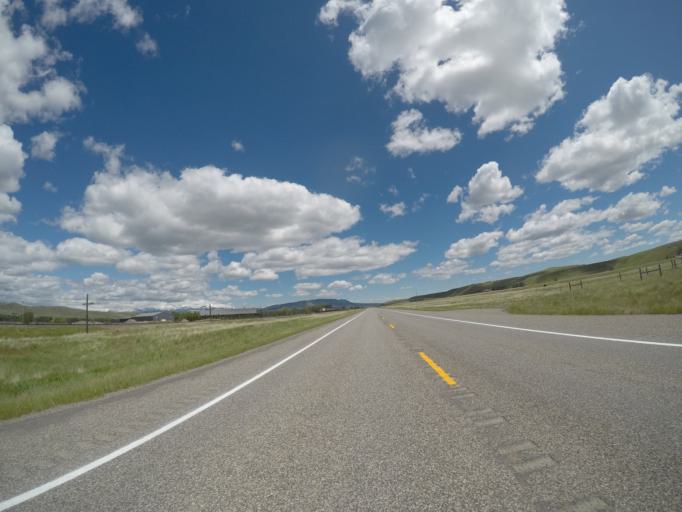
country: US
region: Montana
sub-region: Park County
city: Livingston
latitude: 45.6855
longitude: -110.5100
